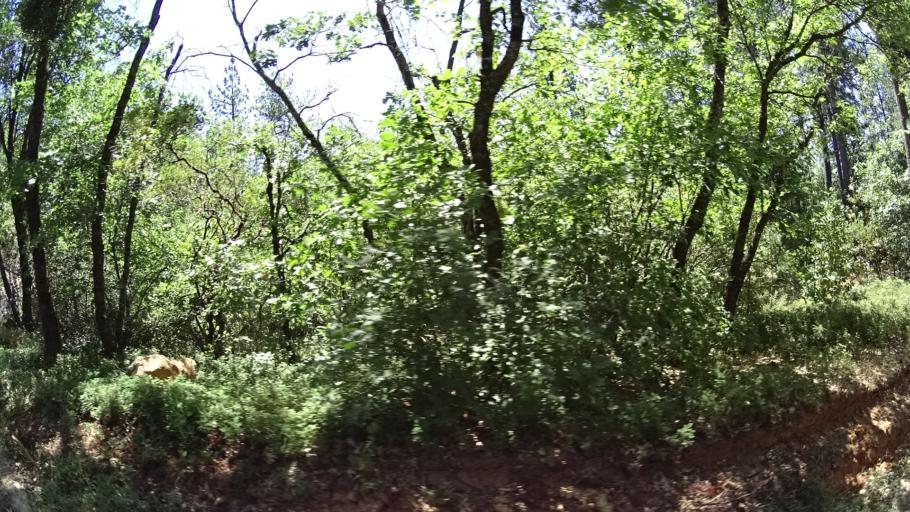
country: US
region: California
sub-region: Amador County
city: Pioneer
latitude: 38.4320
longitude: -120.5051
